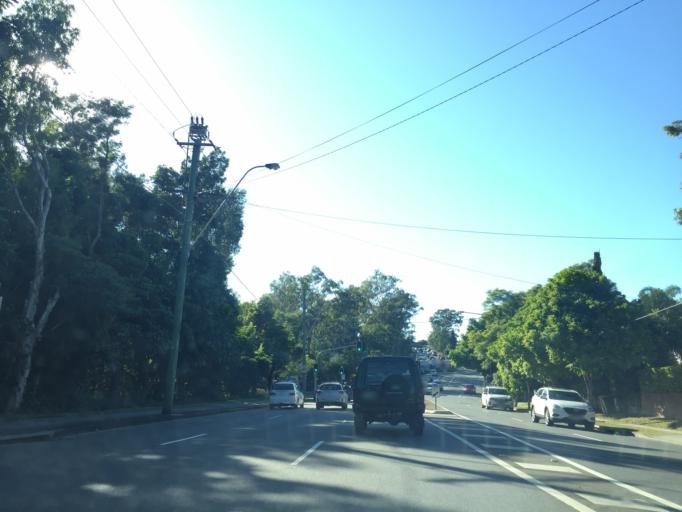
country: AU
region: Queensland
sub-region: Brisbane
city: Milton
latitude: -27.4480
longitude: 152.9733
